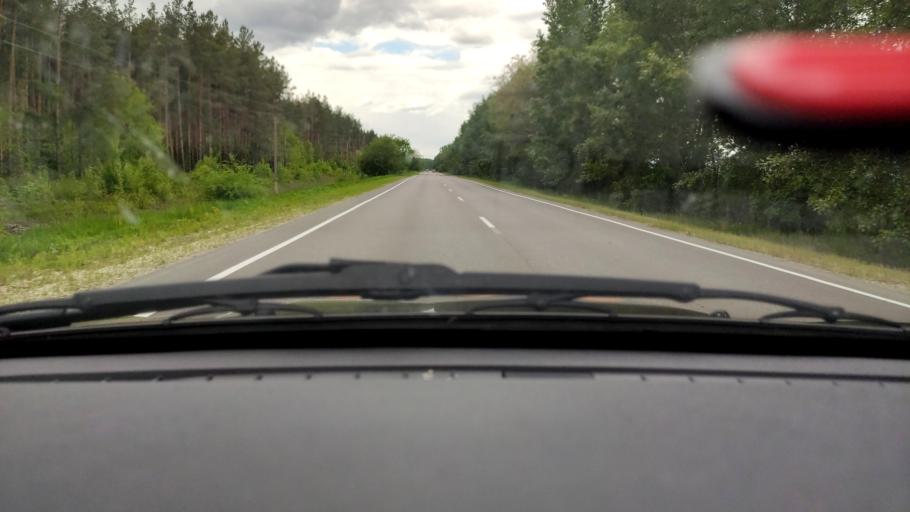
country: RU
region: Belgorod
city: Krasnoye
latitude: 51.0686
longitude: 38.7857
